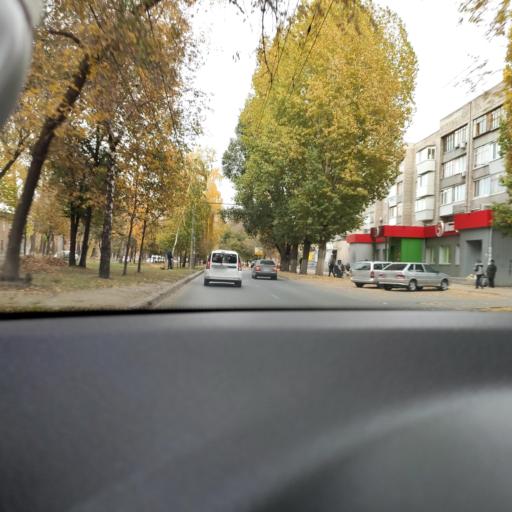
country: RU
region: Samara
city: Samara
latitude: 53.2169
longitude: 50.2381
